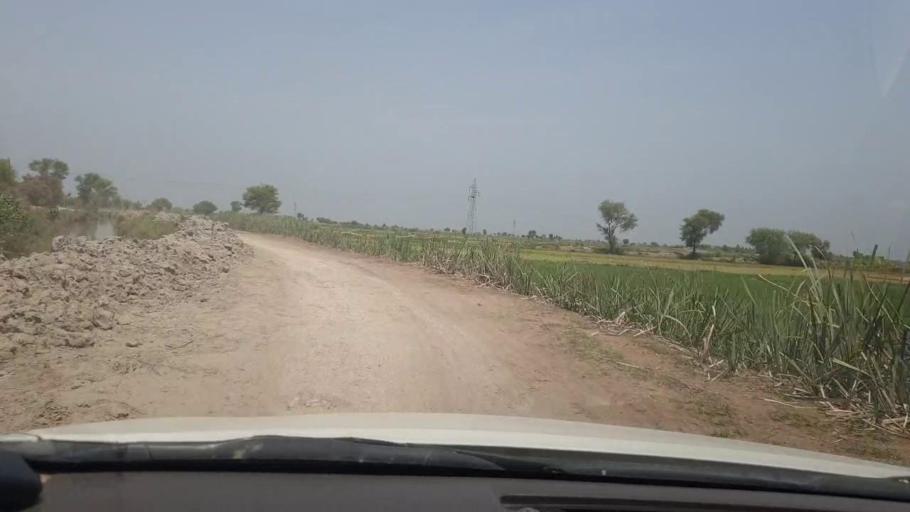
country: PK
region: Sindh
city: Garhi Yasin
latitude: 27.9464
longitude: 68.5285
